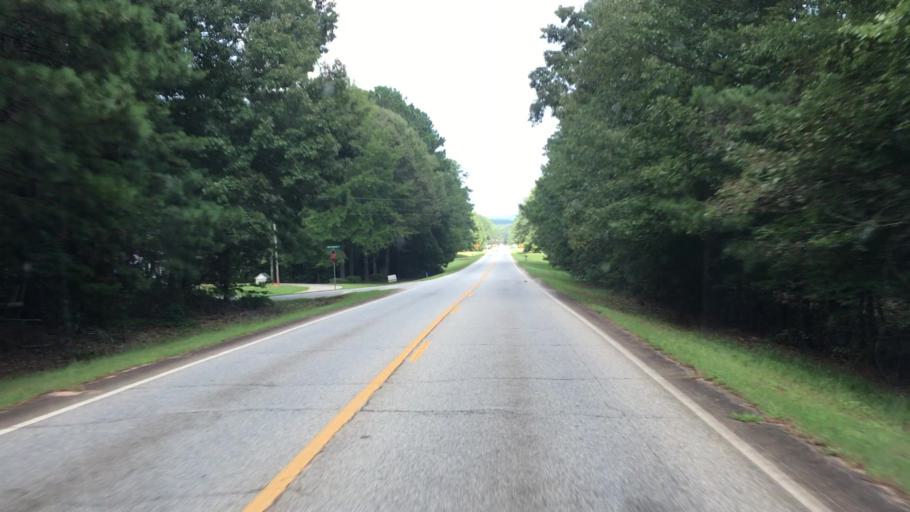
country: US
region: Georgia
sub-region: Butts County
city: Indian Springs
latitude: 33.1506
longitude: -83.8444
